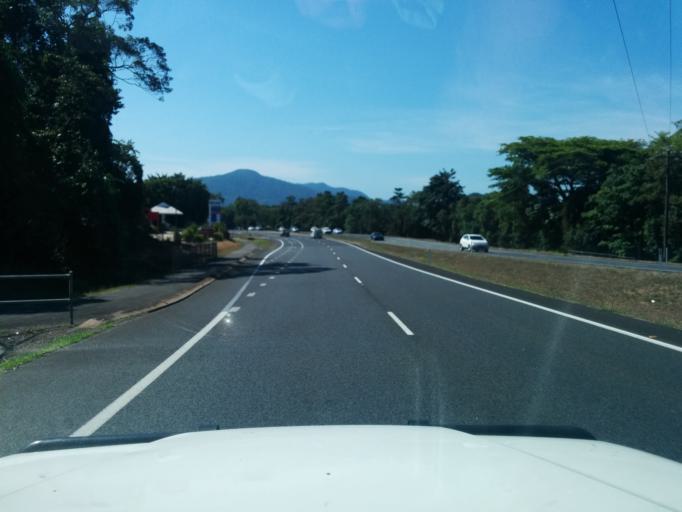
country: AU
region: Queensland
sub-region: Cairns
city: Redlynch
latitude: -16.9075
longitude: 145.7116
